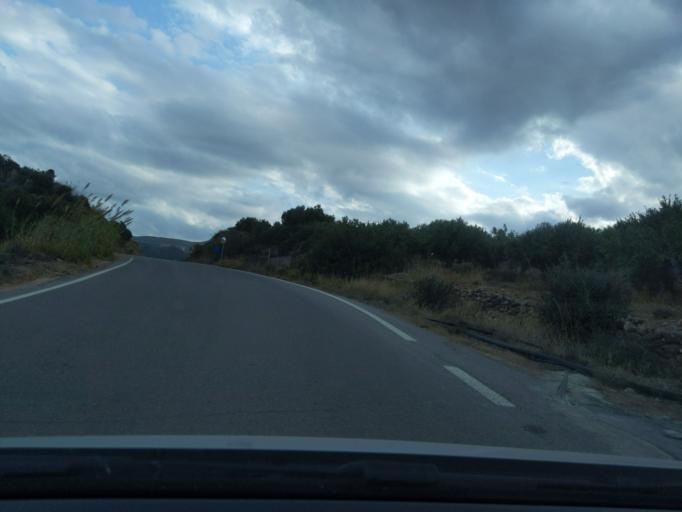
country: GR
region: Crete
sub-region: Nomos Lasithiou
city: Palekastro
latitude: 35.2198
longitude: 26.2583
